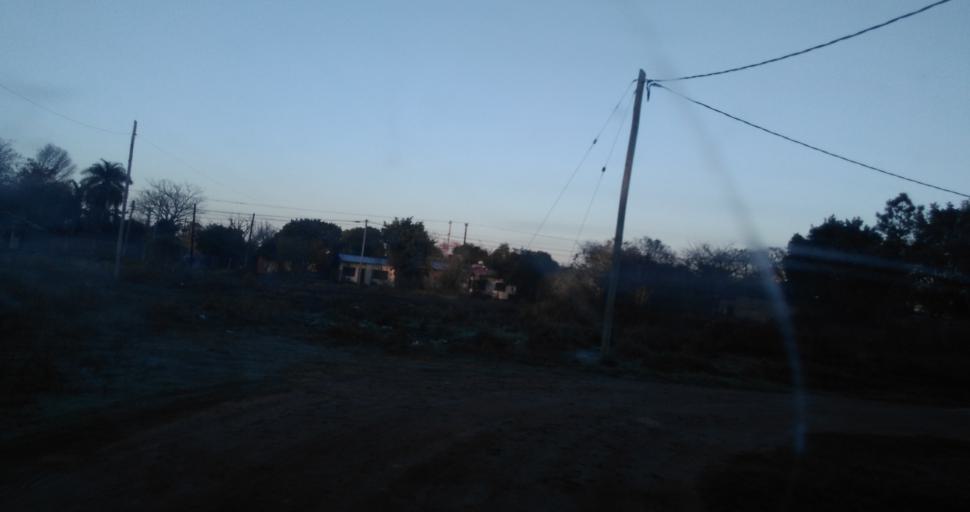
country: AR
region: Chaco
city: Fontana
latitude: -27.4315
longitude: -59.0145
